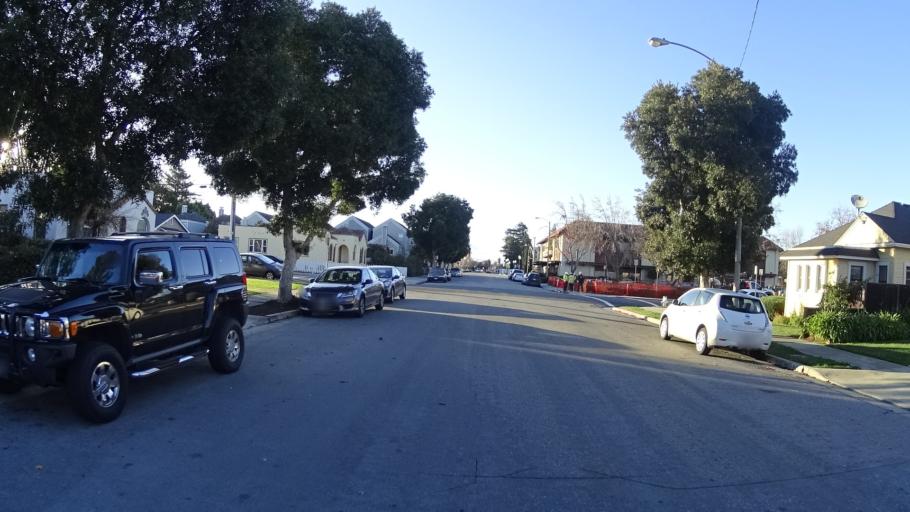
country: US
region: California
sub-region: Santa Clara County
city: Sunnyvale
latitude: 37.3737
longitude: -122.0285
